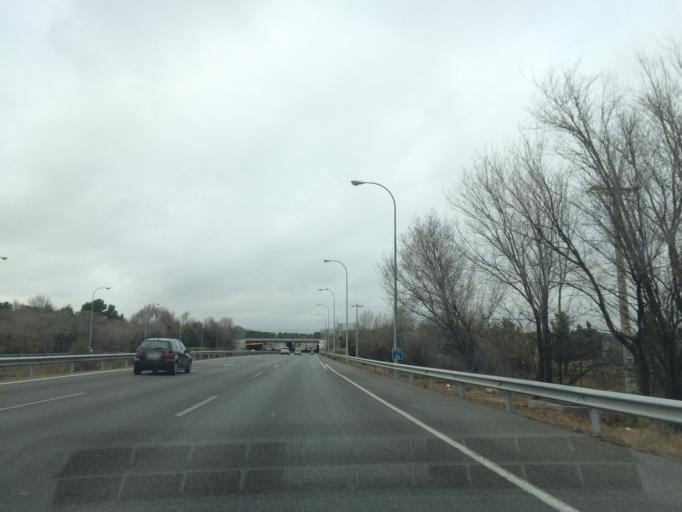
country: ES
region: Madrid
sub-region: Provincia de Madrid
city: Alcorcon
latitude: 40.3686
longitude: -3.7971
